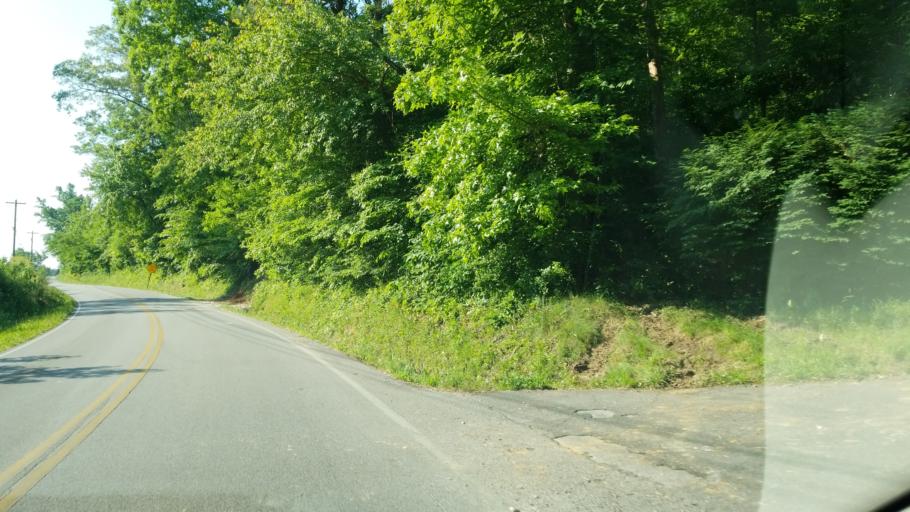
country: US
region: Tennessee
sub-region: Hamilton County
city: Collegedale
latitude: 35.0820
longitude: -85.0092
